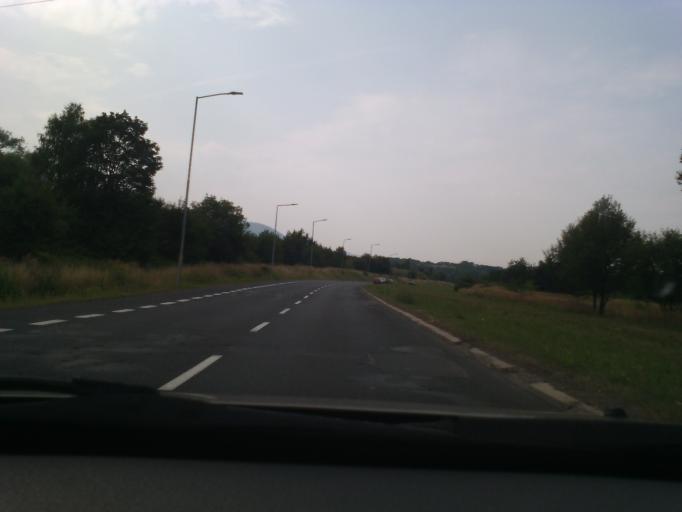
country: PL
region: Lower Silesian Voivodeship
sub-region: Powiat walbrzyski
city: Walbrzych
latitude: 50.7535
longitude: 16.2880
